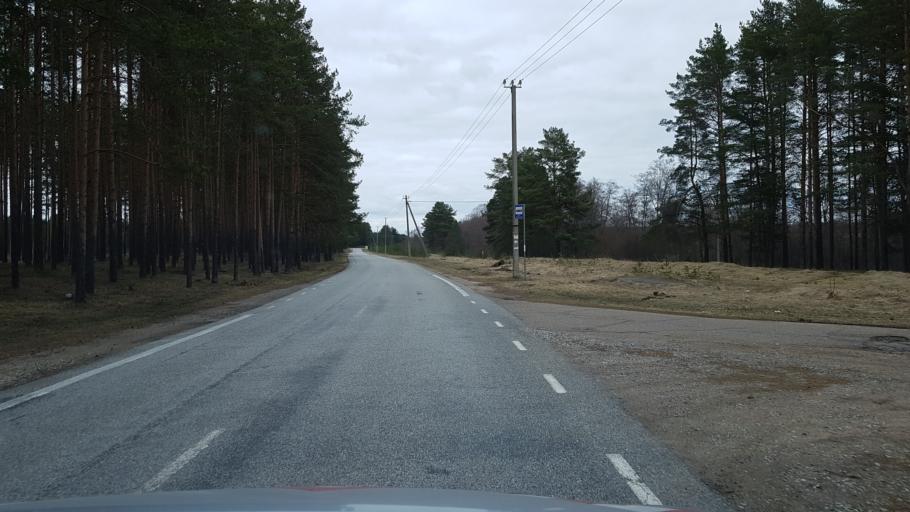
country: EE
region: Ida-Virumaa
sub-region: Narva-Joesuu linn
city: Narva-Joesuu
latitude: 59.4243
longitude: 28.1177
